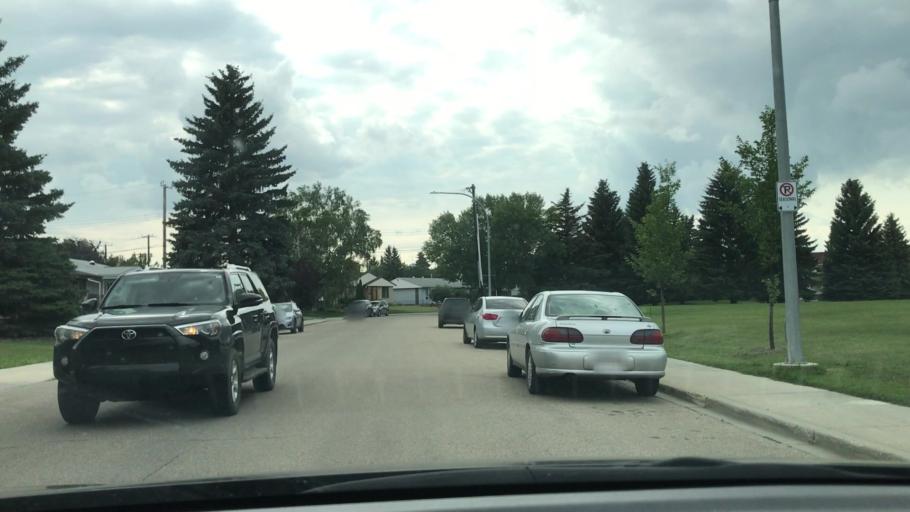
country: CA
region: Alberta
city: Edmonton
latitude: 53.5447
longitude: -113.4250
